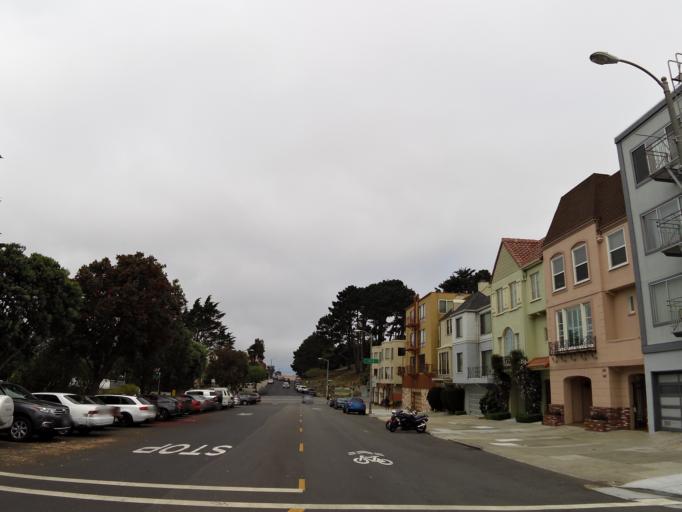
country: US
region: California
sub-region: San Francisco County
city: San Francisco
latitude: 37.7769
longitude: -122.4532
